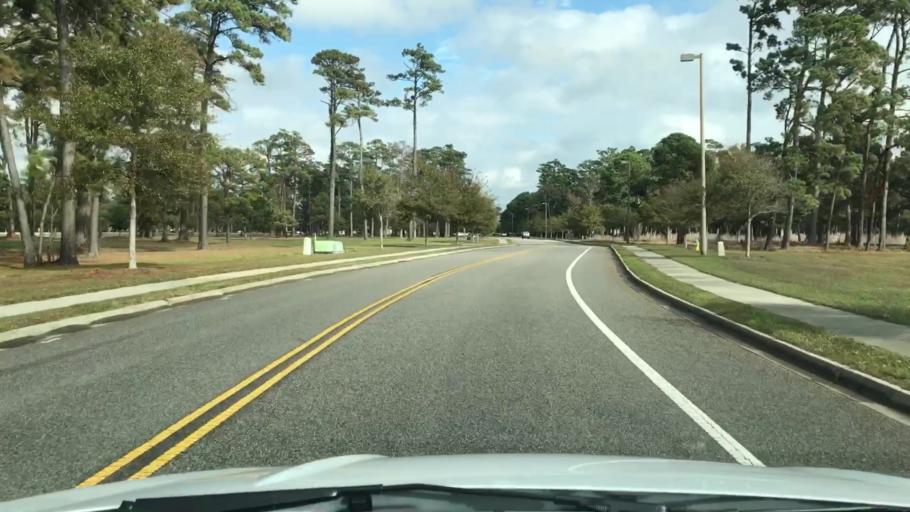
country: US
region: South Carolina
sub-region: Horry County
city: Myrtle Beach
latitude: 33.7224
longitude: -78.8762
